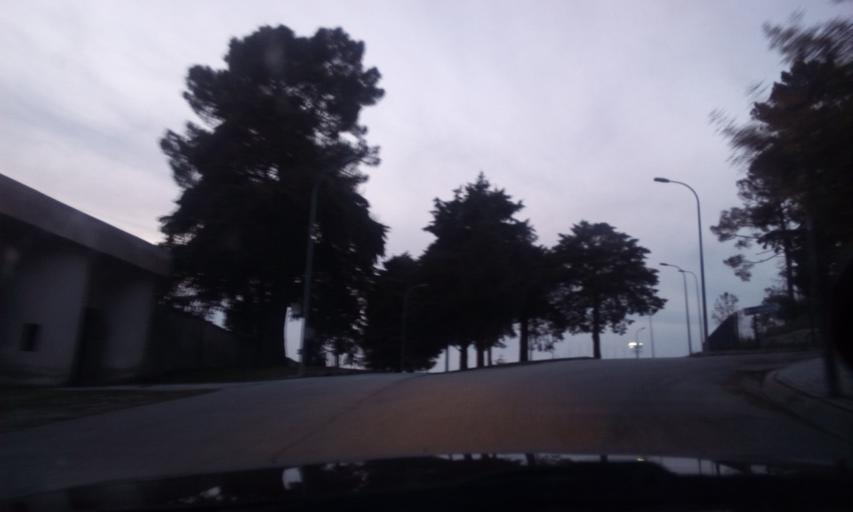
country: PT
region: Guarda
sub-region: Fornos de Algodres
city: Fornos de Algodres
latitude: 40.6217
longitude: -7.5453
